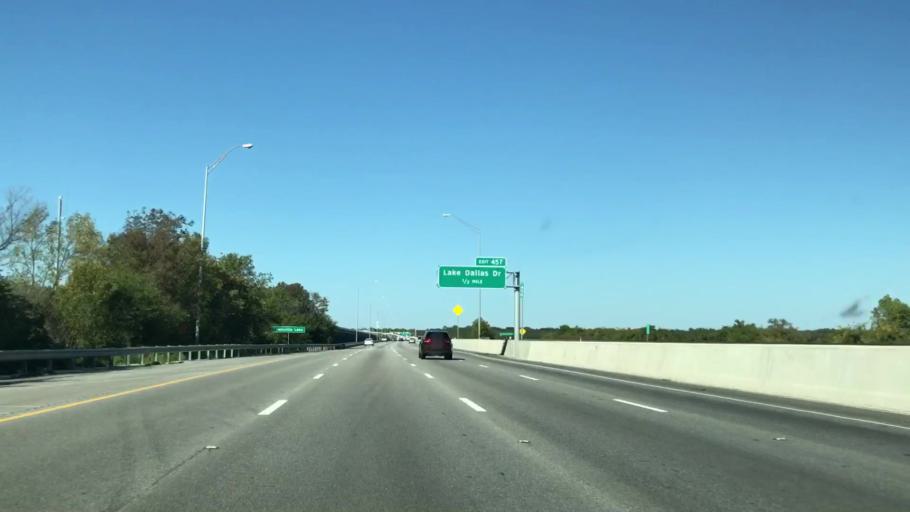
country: US
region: Texas
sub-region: Denton County
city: Highland Village
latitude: 33.0976
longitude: -97.0283
